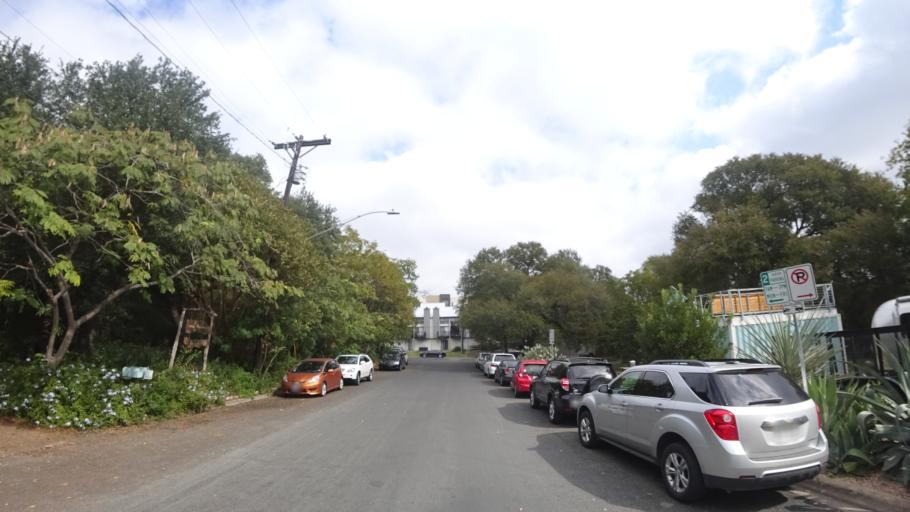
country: US
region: Texas
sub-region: Travis County
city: Austin
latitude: 30.2551
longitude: -97.7609
